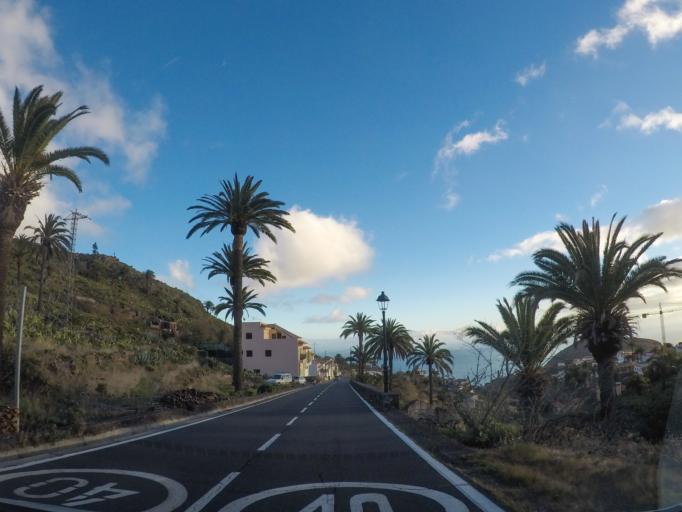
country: ES
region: Canary Islands
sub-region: Provincia de Santa Cruz de Tenerife
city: Alajero
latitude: 28.0656
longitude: -17.2377
